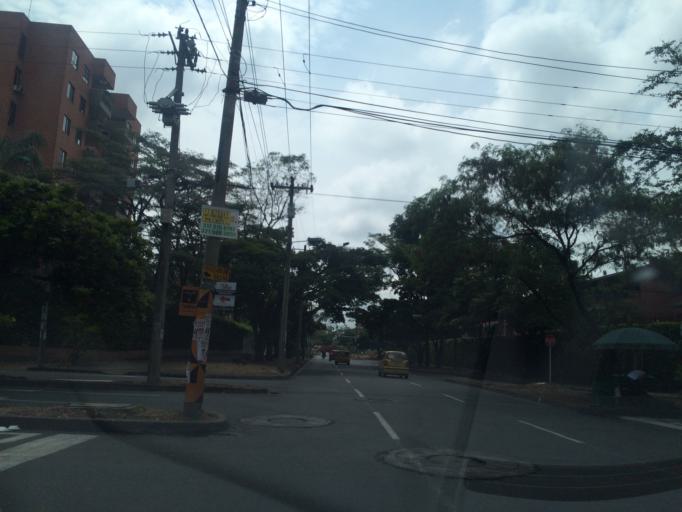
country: CO
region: Valle del Cauca
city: Cali
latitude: 3.3795
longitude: -76.5268
